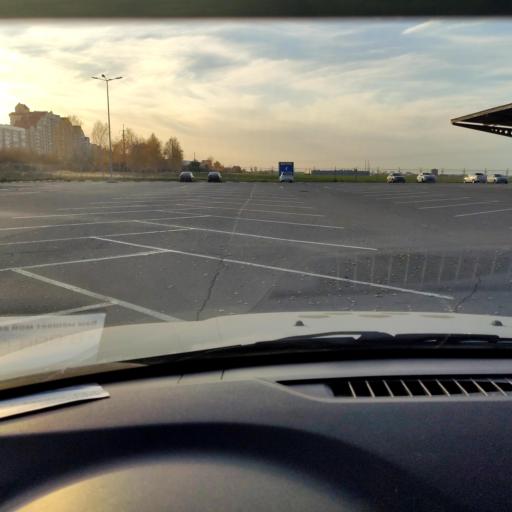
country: RU
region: Samara
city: Tol'yatti
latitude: 53.5468
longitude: 49.3733
